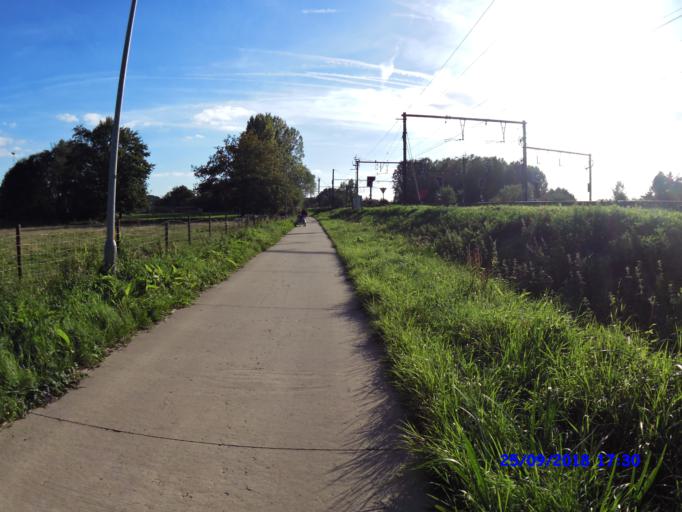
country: BE
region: Flanders
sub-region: Provincie Vlaams-Brabant
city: Aarschot
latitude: 50.9953
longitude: 4.8324
